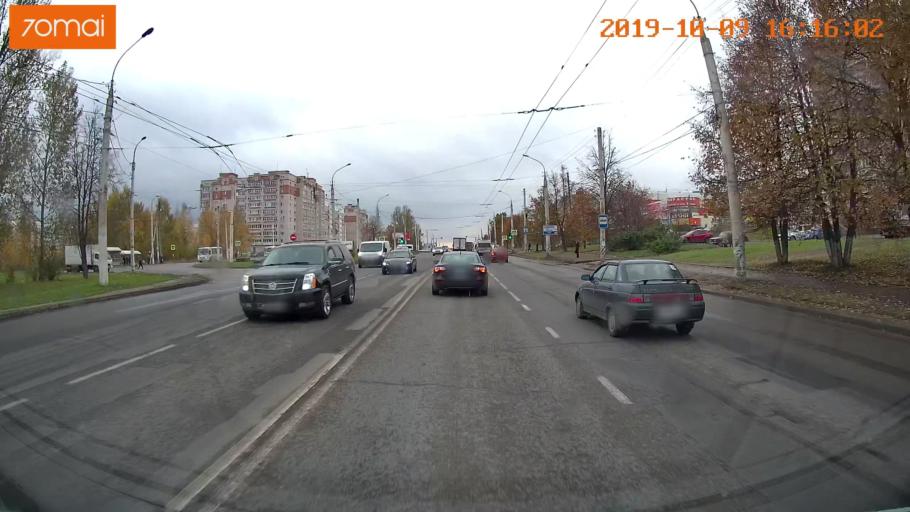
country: RU
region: Kostroma
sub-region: Kostromskoy Rayon
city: Kostroma
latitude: 57.7370
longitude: 40.9119
